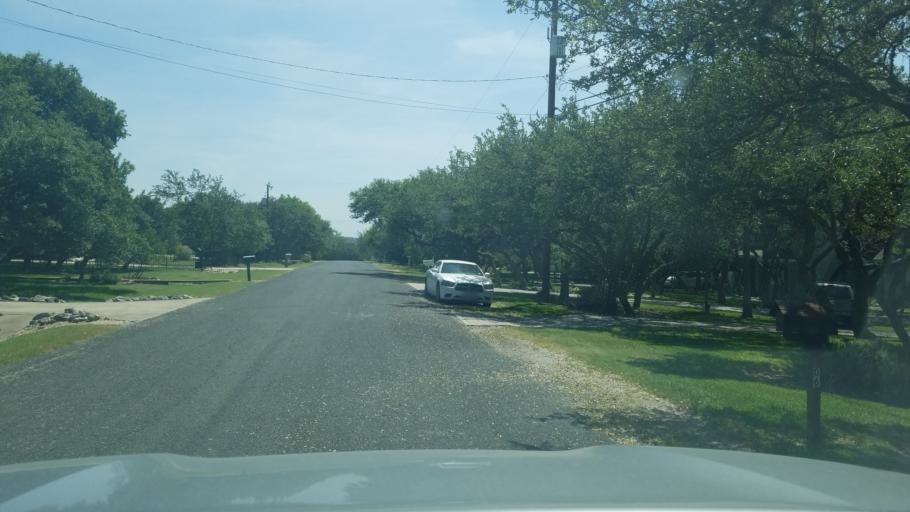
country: US
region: Texas
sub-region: Bexar County
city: Timberwood Park
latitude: 29.7004
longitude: -98.4886
